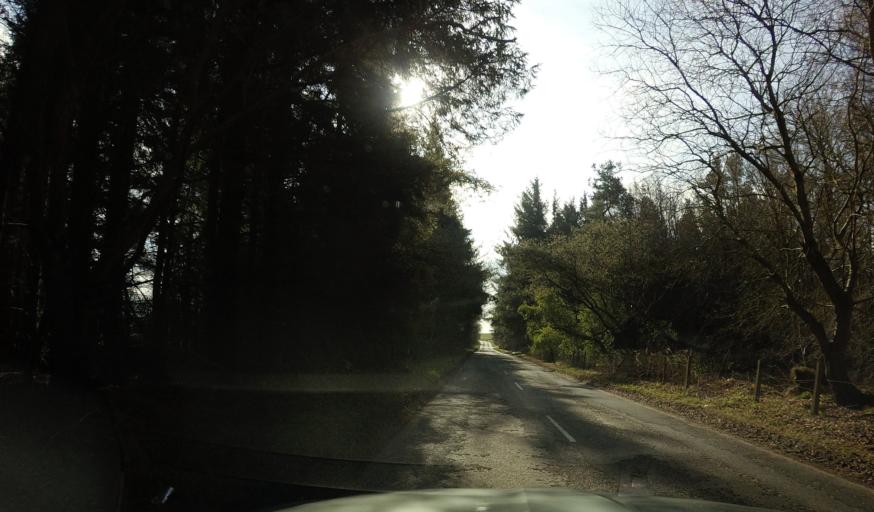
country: GB
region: Scotland
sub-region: Midlothian
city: Penicuik
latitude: 55.8145
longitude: -3.1947
